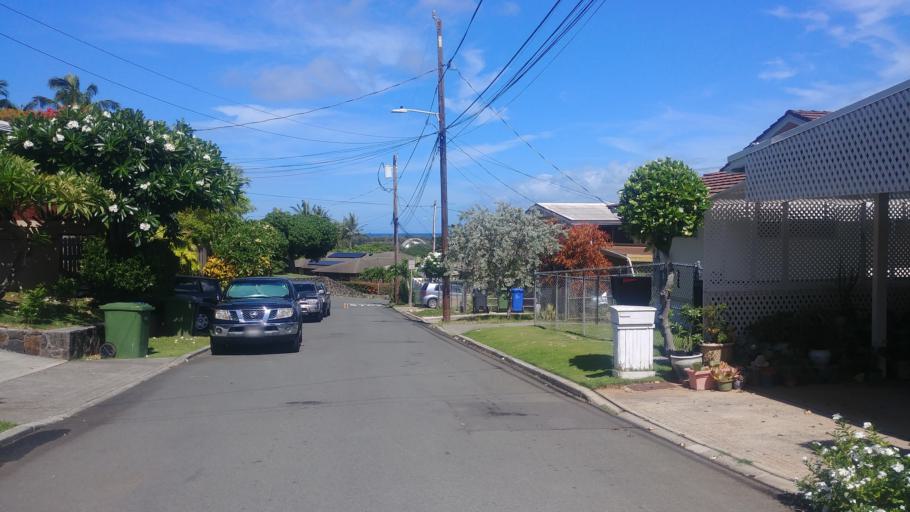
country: US
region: Hawaii
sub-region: Honolulu County
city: Honolulu
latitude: 21.2685
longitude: -157.8097
